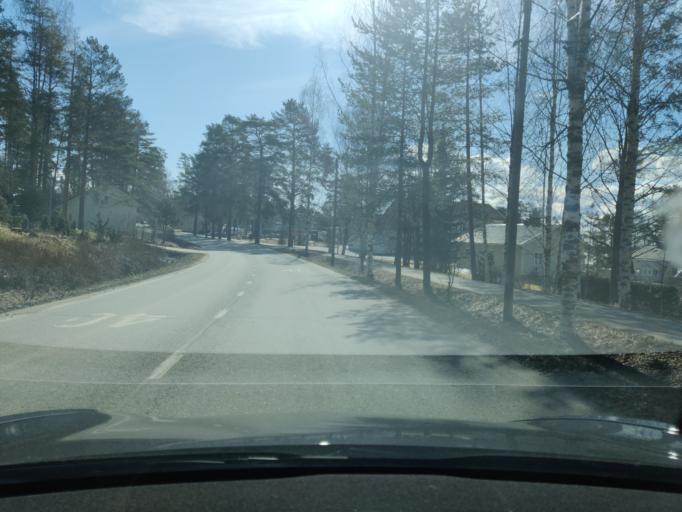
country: FI
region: Northern Savo
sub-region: Kuopio
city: Vehmersalmi
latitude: 62.7630
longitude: 28.0230
